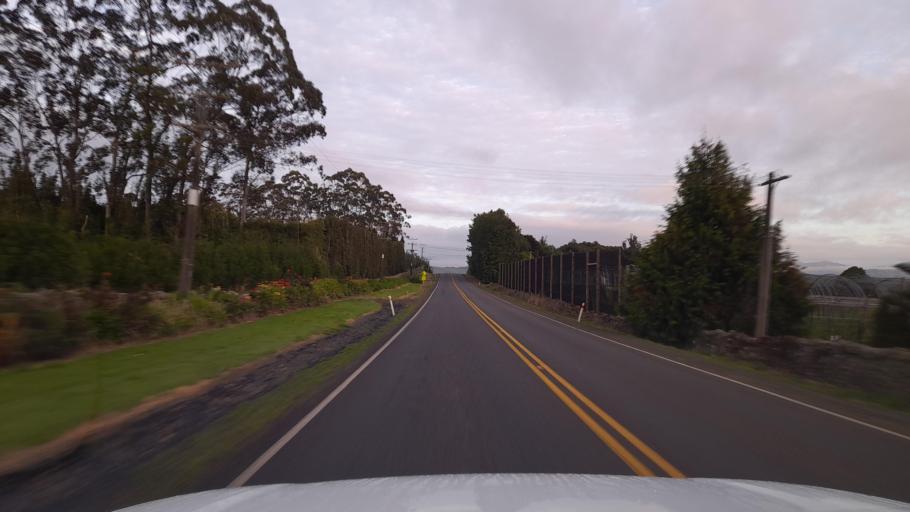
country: NZ
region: Northland
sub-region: Whangarei
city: Maungatapere
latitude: -35.7461
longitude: 174.1568
